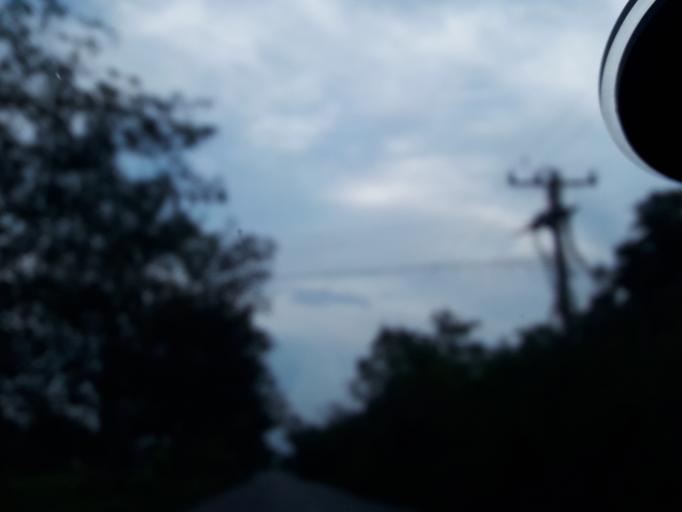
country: TH
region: Pathum Thani
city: Nong Suea
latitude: 14.1157
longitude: 100.8685
